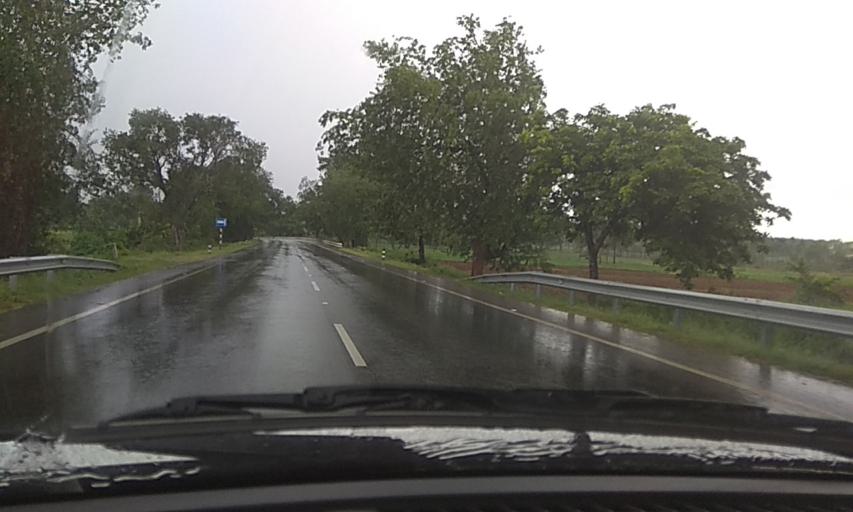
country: IN
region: Karnataka
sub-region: Mandya
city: Maddur
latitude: 12.7626
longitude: 77.0597
